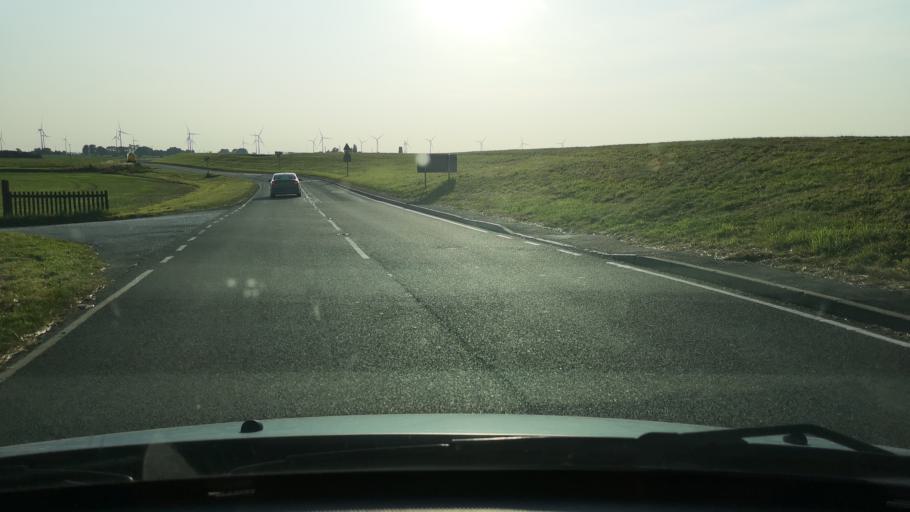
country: GB
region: England
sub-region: East Riding of Yorkshire
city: Skelton
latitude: 53.6866
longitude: -0.8432
